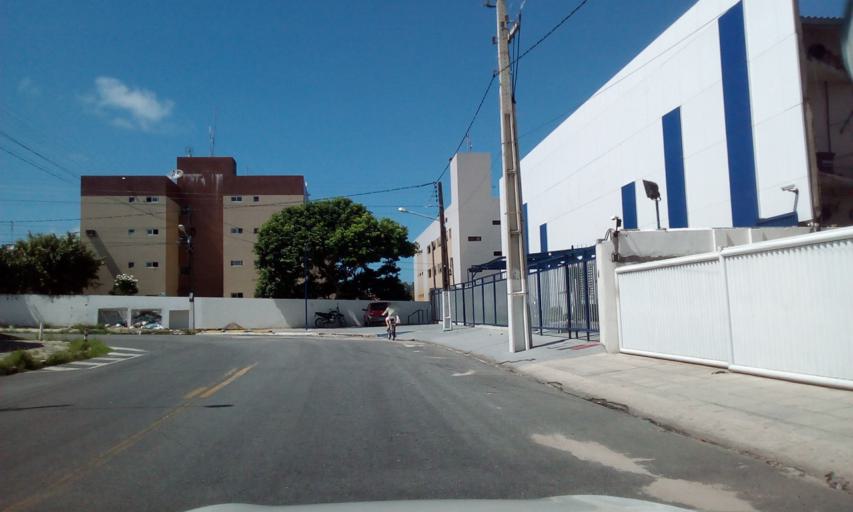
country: BR
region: Paraiba
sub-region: Joao Pessoa
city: Joao Pessoa
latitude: -7.1871
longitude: -34.8436
